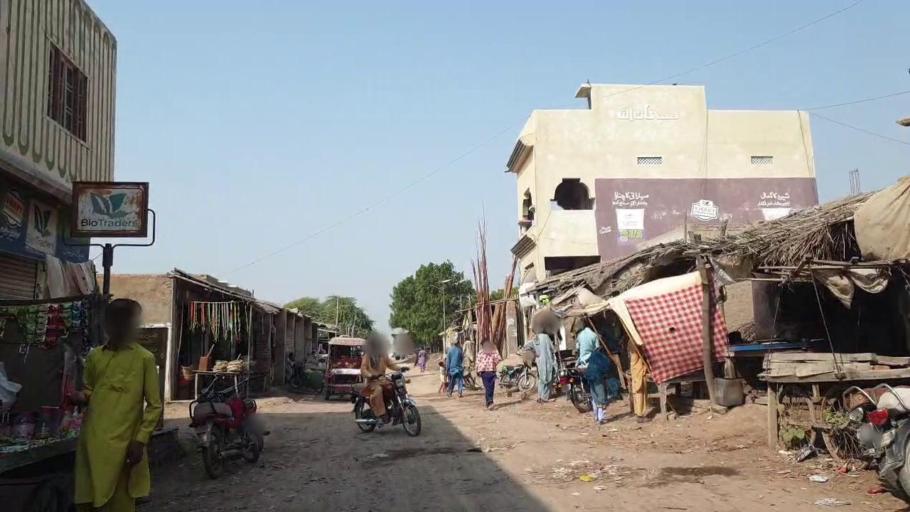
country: PK
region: Sindh
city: Kario
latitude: 24.9277
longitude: 68.5609
